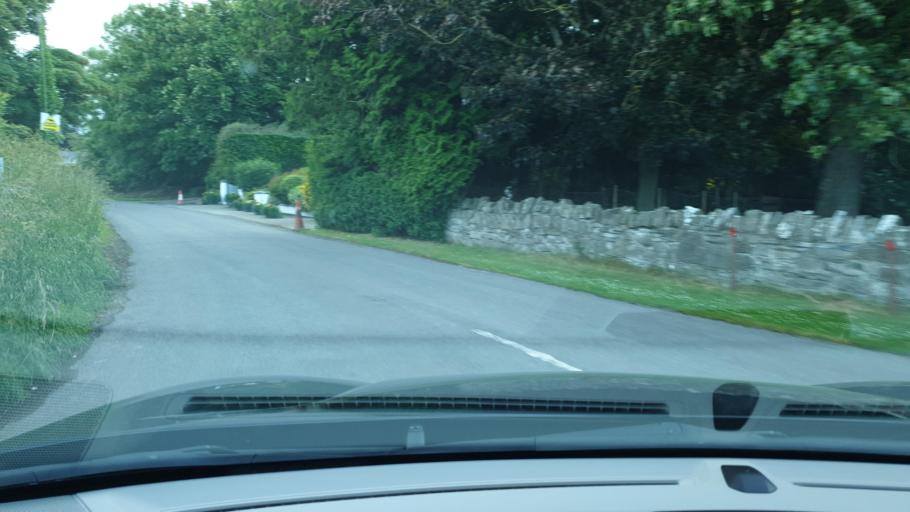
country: IE
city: Kentstown
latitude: 53.5734
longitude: -6.4960
